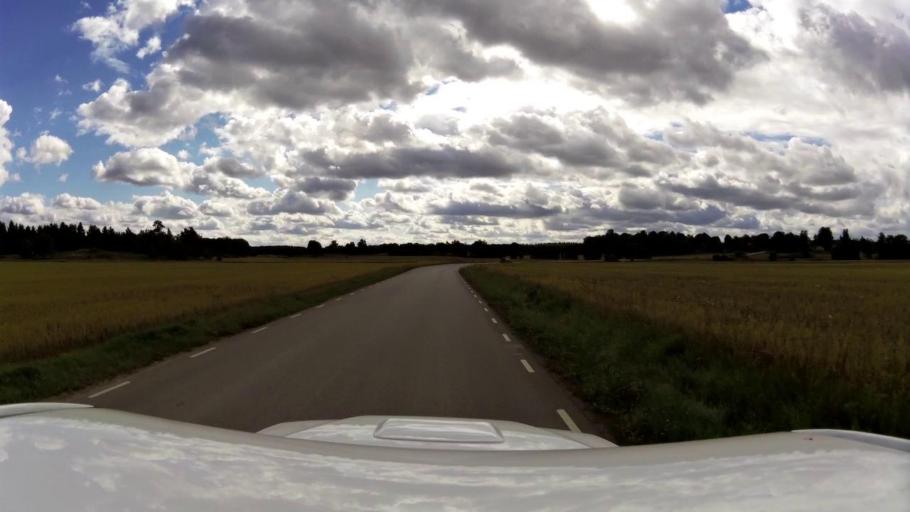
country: SE
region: OEstergoetland
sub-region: Linkopings Kommun
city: Linkoping
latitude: 58.3774
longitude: 15.5943
